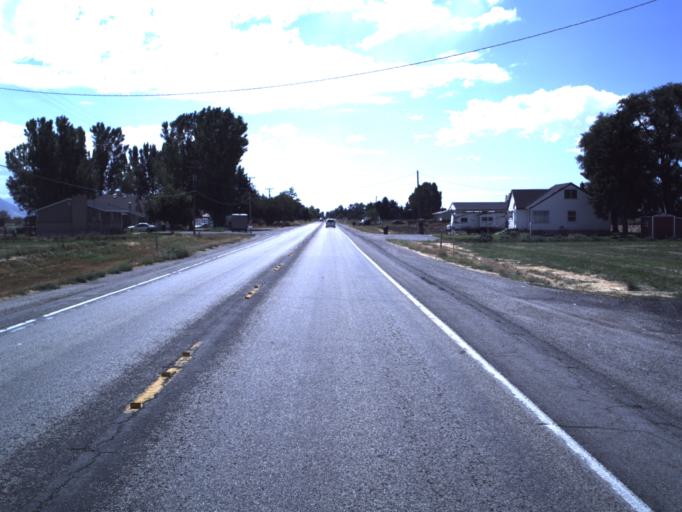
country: US
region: Utah
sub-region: Box Elder County
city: Garland
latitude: 41.8118
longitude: -112.1452
